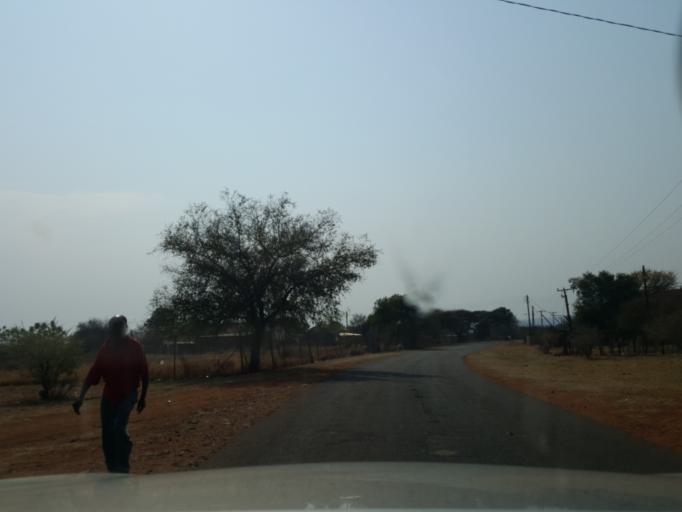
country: BW
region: South East
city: Lobatse
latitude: -25.2878
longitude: 25.9019
